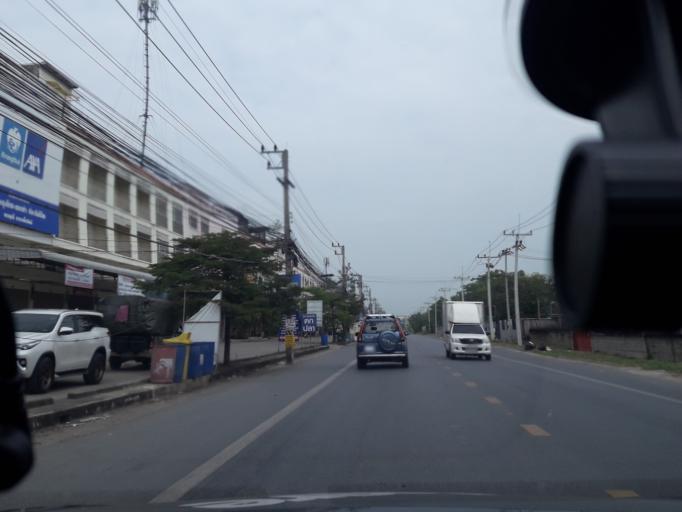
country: TH
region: Pathum Thani
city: Ban Rangsit
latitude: 14.0216
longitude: 100.7535
